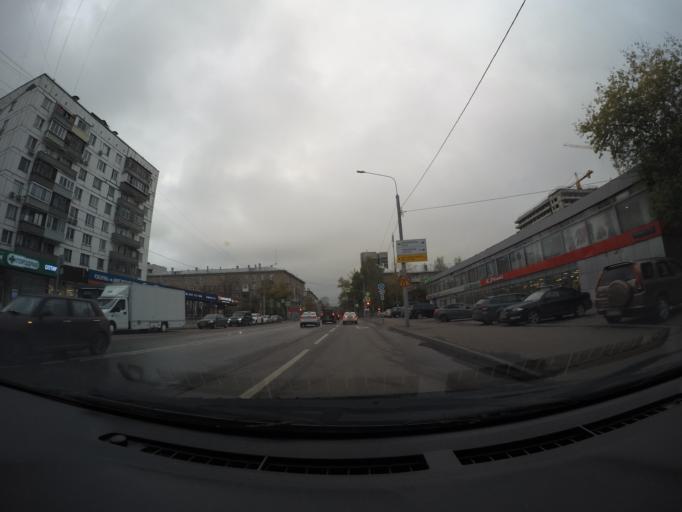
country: RU
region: Moscow
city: Perovo
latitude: 55.7590
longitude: 37.7949
